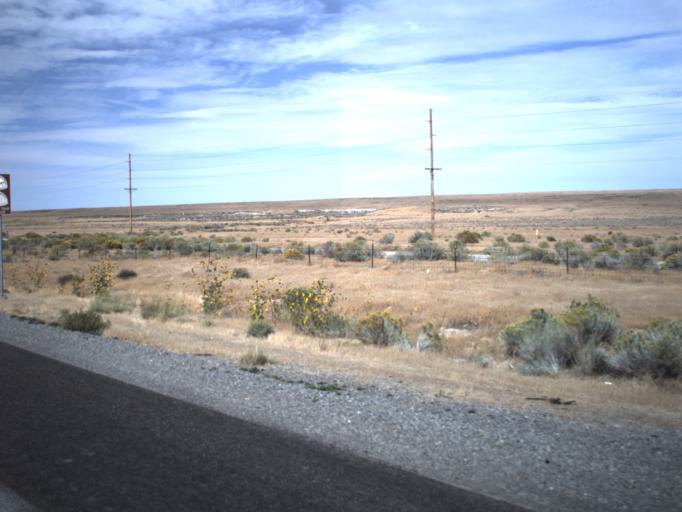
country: US
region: Utah
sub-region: Tooele County
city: Grantsville
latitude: 40.7652
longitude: -112.9945
